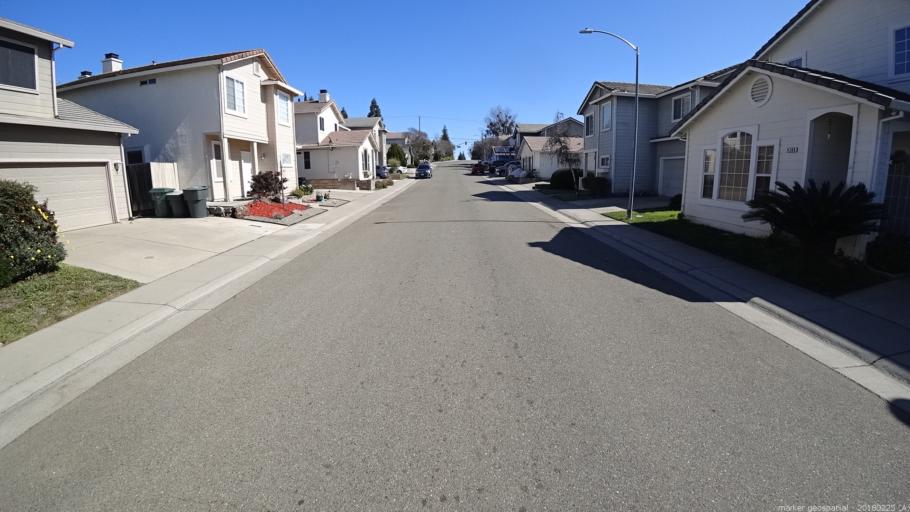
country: US
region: California
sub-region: Sacramento County
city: North Highlands
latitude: 38.7168
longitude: -121.3664
